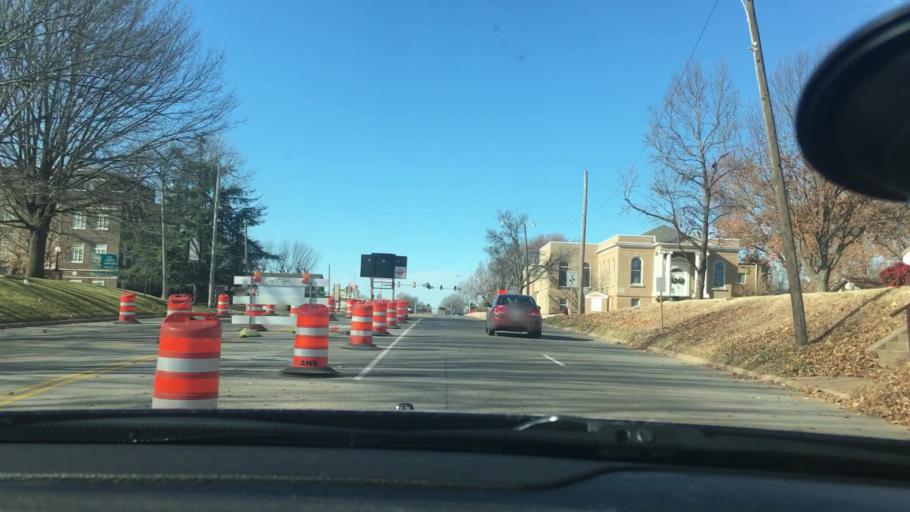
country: US
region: Oklahoma
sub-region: McClain County
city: Purcell
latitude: 35.0136
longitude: -97.3601
